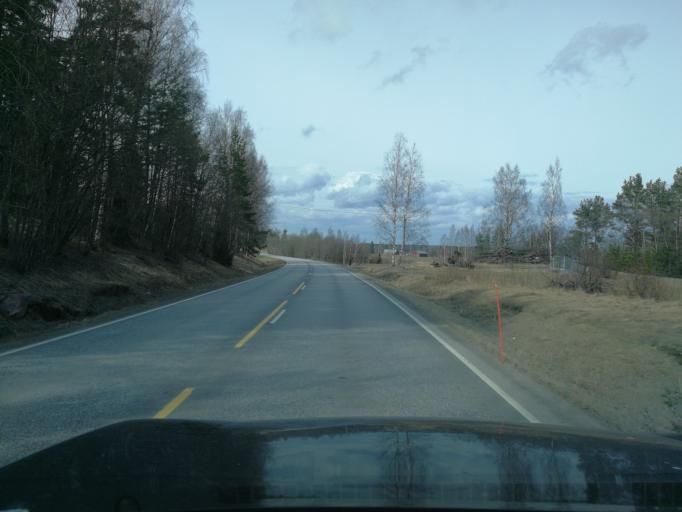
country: FI
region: Uusimaa
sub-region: Helsinki
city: Siuntio
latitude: 60.1054
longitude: 24.2473
